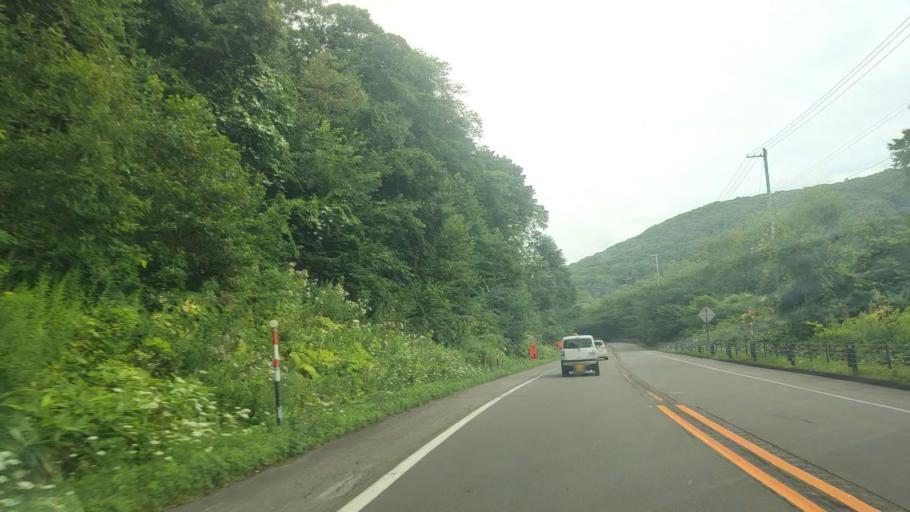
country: JP
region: Hokkaido
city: Nanae
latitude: 41.9733
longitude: 140.6473
